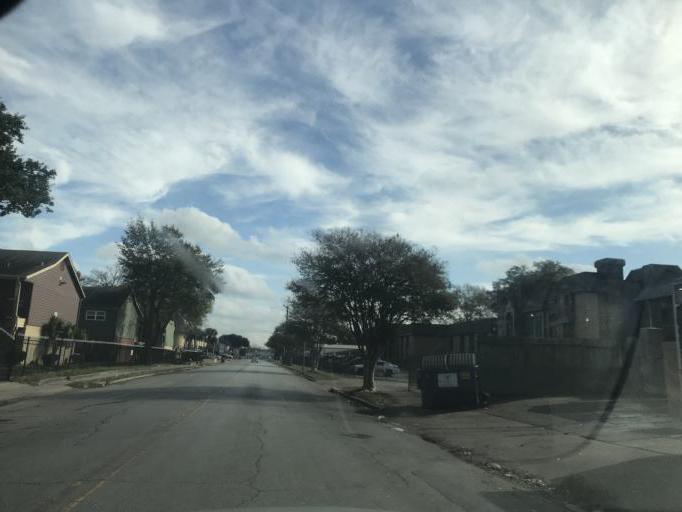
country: US
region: Texas
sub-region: Harris County
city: Piney Point Village
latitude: 29.7258
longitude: -95.4992
